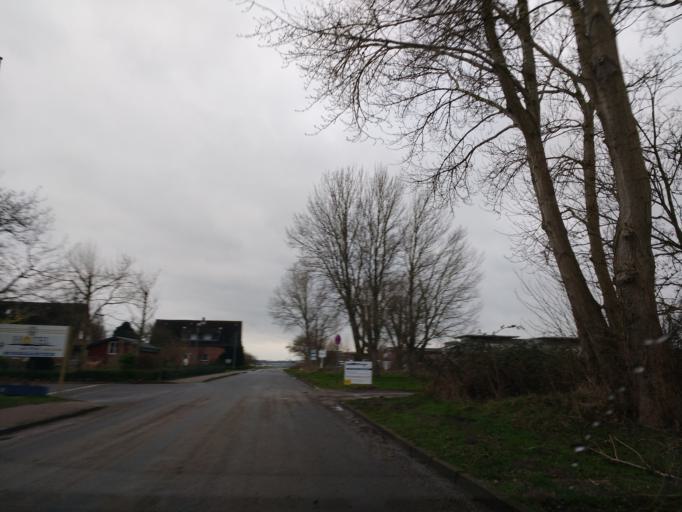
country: DE
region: Schleswig-Holstein
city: Grossenbrode
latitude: 54.3558
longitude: 11.0824
